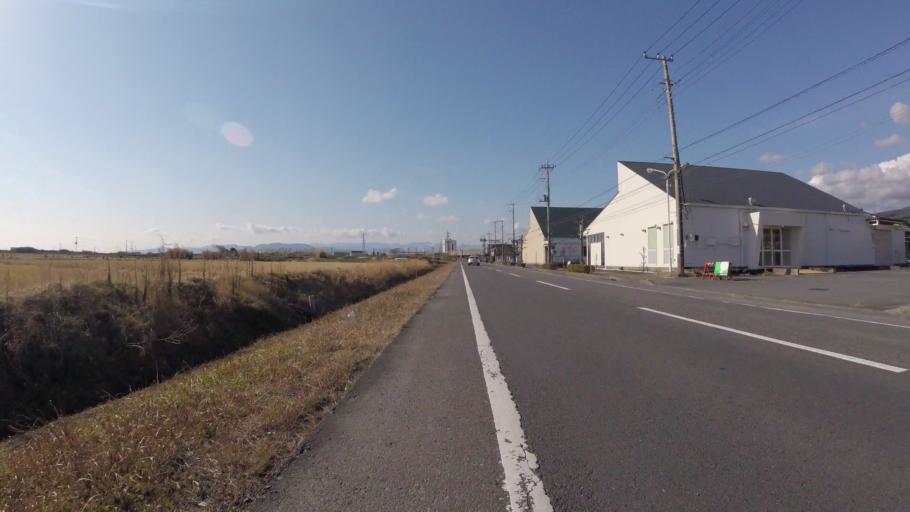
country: JP
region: Shizuoka
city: Fuji
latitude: 35.1544
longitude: 138.7525
